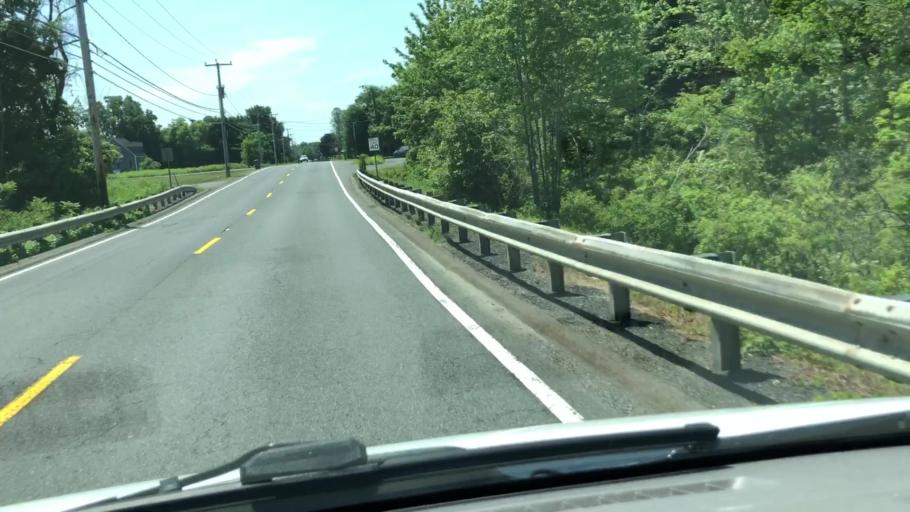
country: US
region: Massachusetts
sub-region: Franklin County
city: Whately
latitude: 42.4401
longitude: -72.6247
